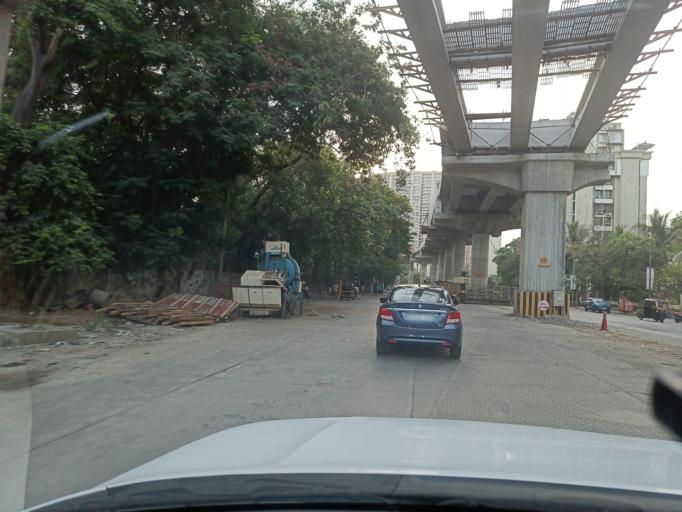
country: IN
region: Maharashtra
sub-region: Mumbai Suburban
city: Powai
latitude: 19.1394
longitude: 72.8240
